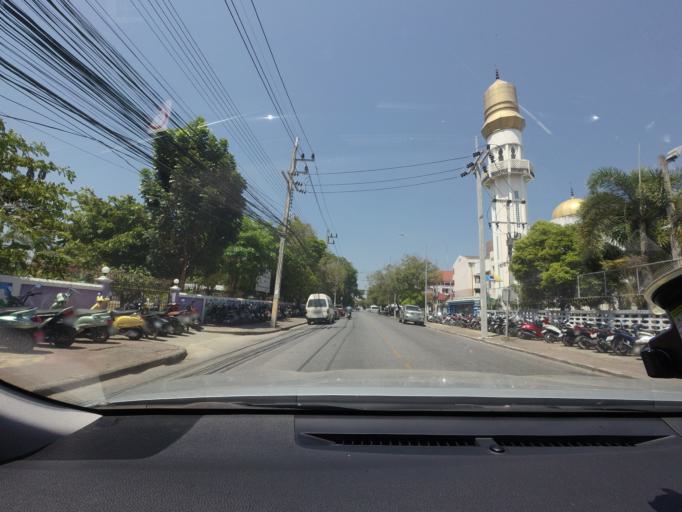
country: TH
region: Yala
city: Yala
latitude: 6.5410
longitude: 101.2848
